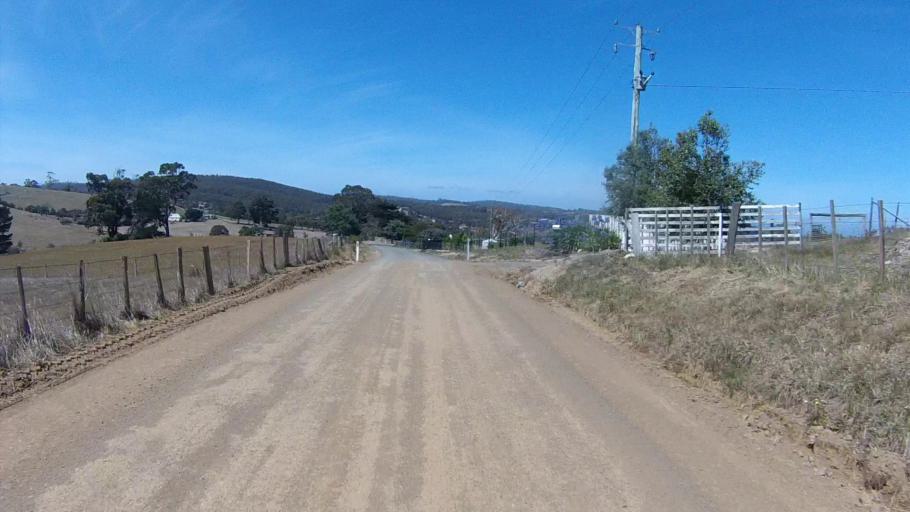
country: AU
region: Tasmania
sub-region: Sorell
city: Sorell
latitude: -42.7932
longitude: 147.6392
